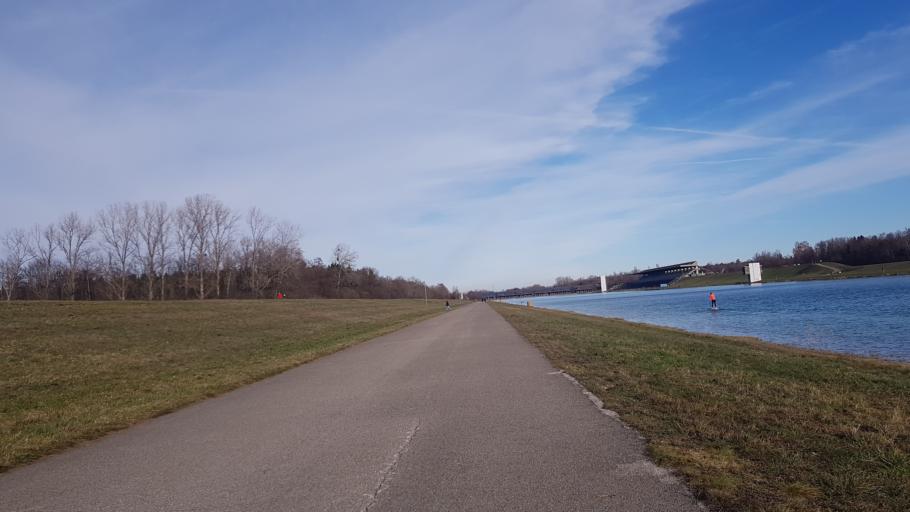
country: DE
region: Bavaria
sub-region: Upper Bavaria
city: Oberschleissheim
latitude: 48.2434
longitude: 11.5145
